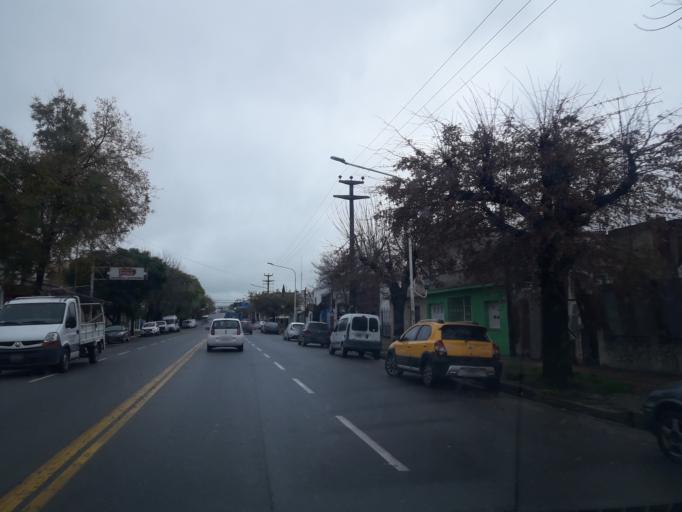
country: AR
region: Buenos Aires
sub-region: Partido de Tandil
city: Tandil
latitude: -37.3209
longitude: -59.1501
